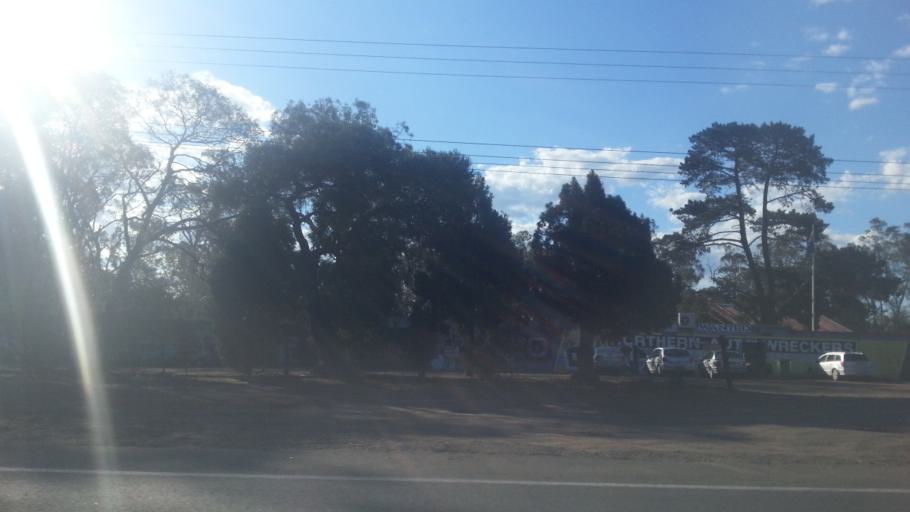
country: AU
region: New South Wales
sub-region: Penrith Municipality
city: Werrington Downs
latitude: -33.6784
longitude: 150.7440
